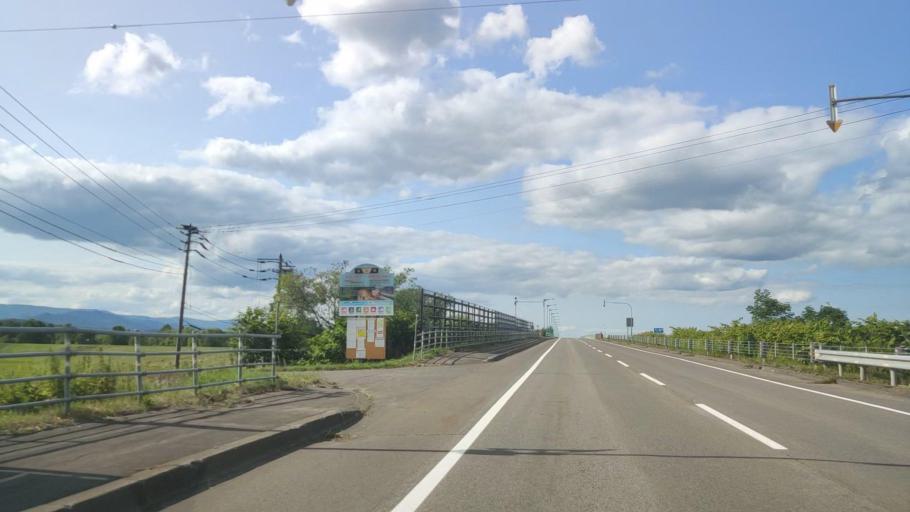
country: JP
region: Hokkaido
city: Nayoro
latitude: 44.4520
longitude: 142.3606
